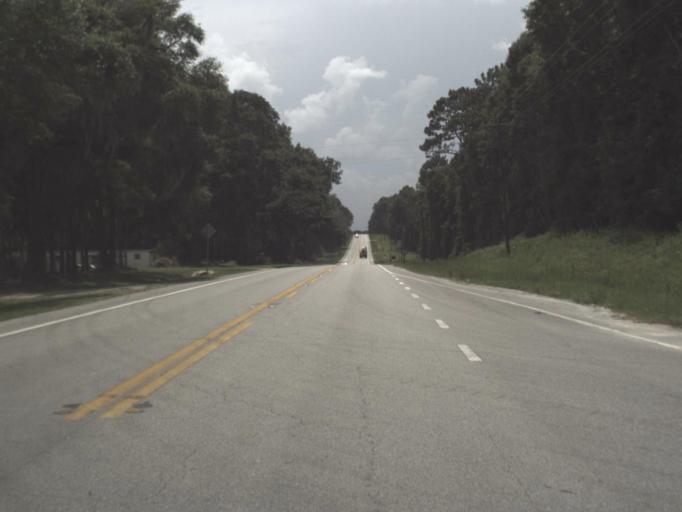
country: US
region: Florida
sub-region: Madison County
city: Madison
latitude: 30.4719
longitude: -83.3620
